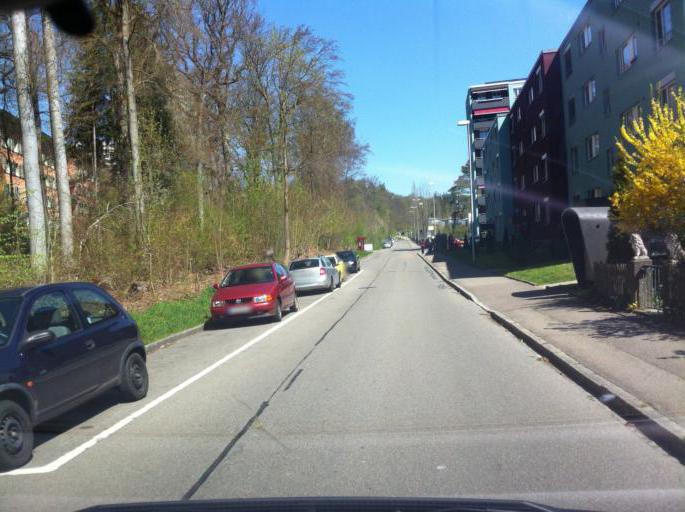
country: CH
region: Schaffhausen
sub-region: Bezirk Schaffhausen
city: Schaffhausen
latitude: 47.7099
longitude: 8.6370
